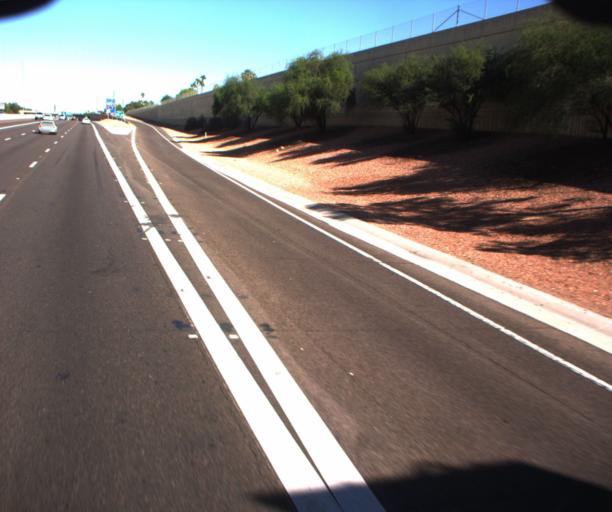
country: US
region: Arizona
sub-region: Maricopa County
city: San Carlos
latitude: 33.3581
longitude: -111.8942
